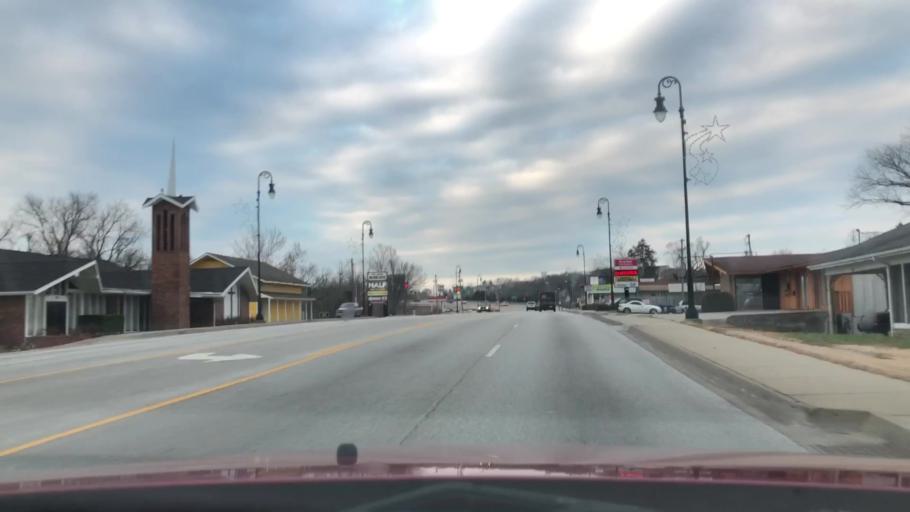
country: US
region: Missouri
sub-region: Taney County
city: Branson
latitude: 36.6524
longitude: -93.2204
